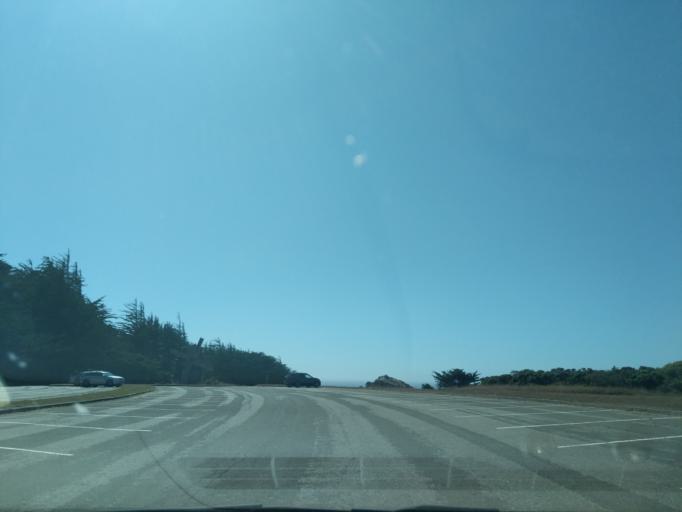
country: US
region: California
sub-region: Sonoma County
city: Monte Rio
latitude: 38.5161
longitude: -123.2471
